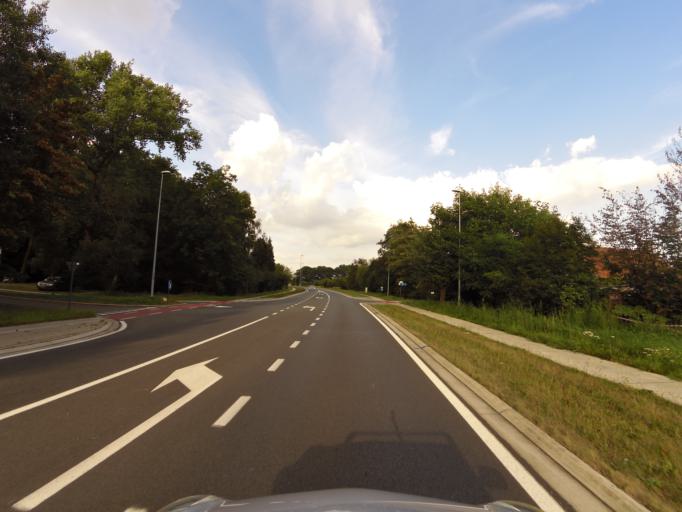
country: BE
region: Flanders
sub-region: Provincie Oost-Vlaanderen
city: Nazareth
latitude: 50.9905
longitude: 3.5921
